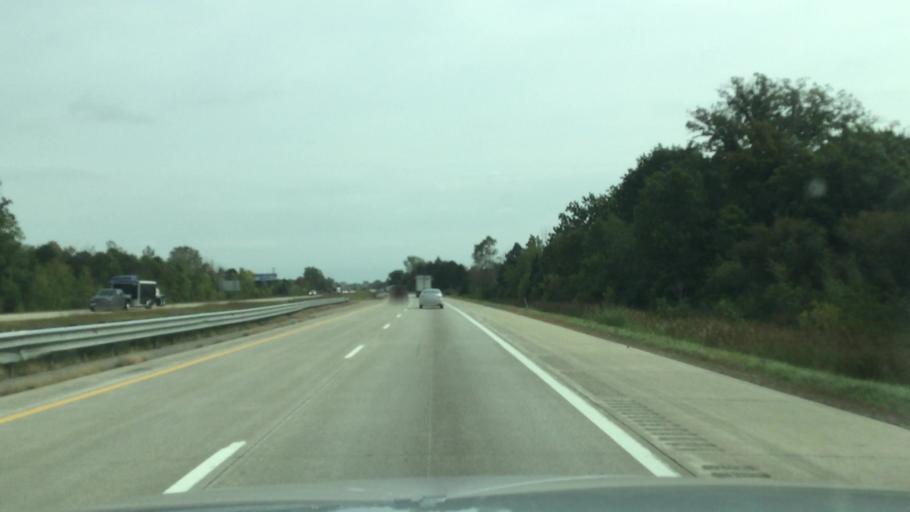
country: US
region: Michigan
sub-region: Genesee County
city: Swartz Creek
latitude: 42.9660
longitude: -83.7875
